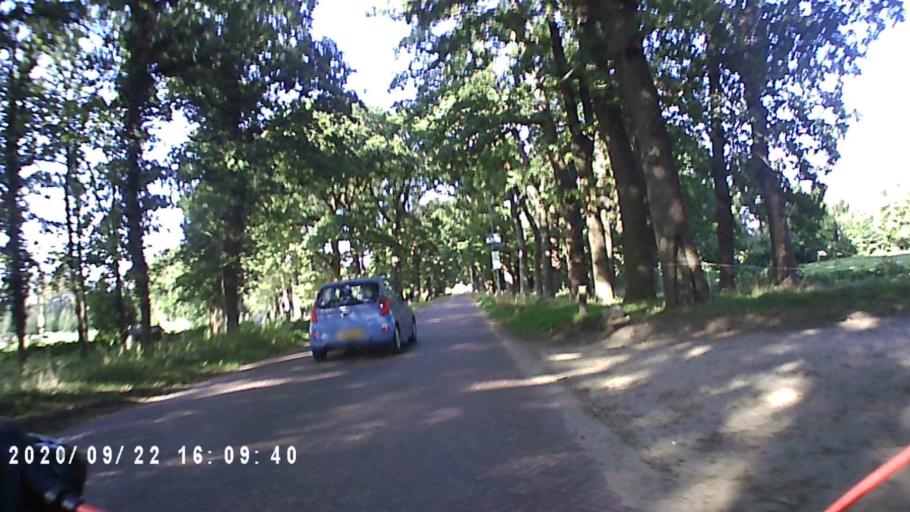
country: NL
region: Drenthe
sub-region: Gemeente Assen
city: Assen
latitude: 53.0500
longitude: 6.4432
